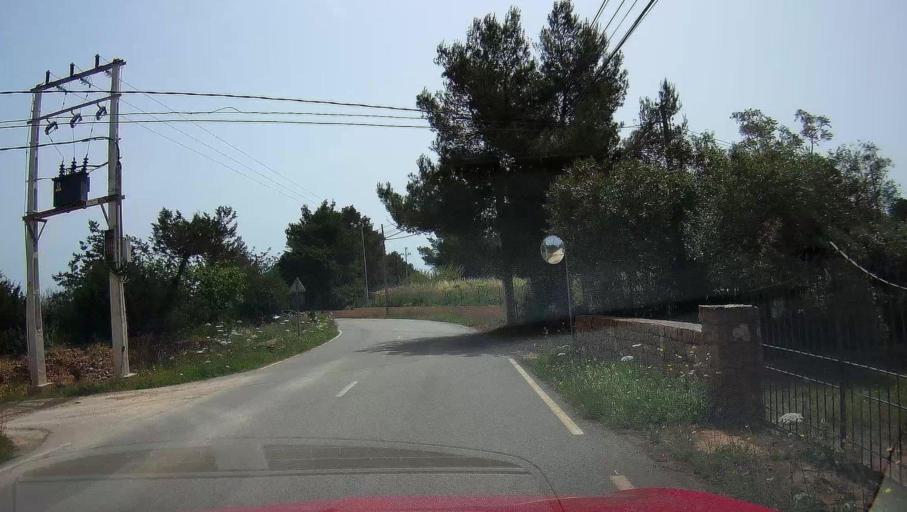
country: ES
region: Balearic Islands
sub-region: Illes Balears
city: Santa Eularia des Riu
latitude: 39.0111
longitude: 1.5660
